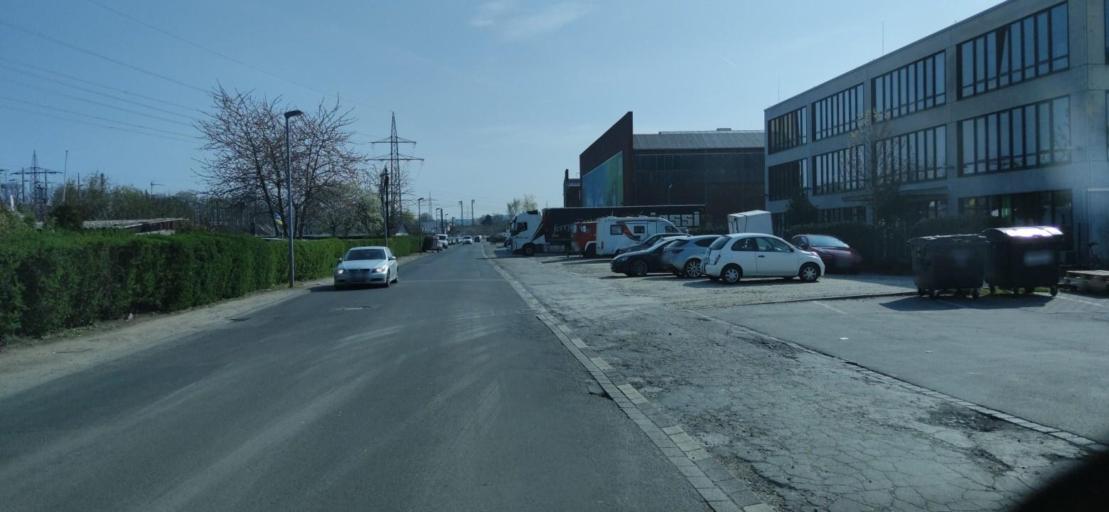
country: DE
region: North Rhine-Westphalia
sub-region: Regierungsbezirk Dusseldorf
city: Dusseldorf
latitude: 51.2207
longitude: 6.8341
